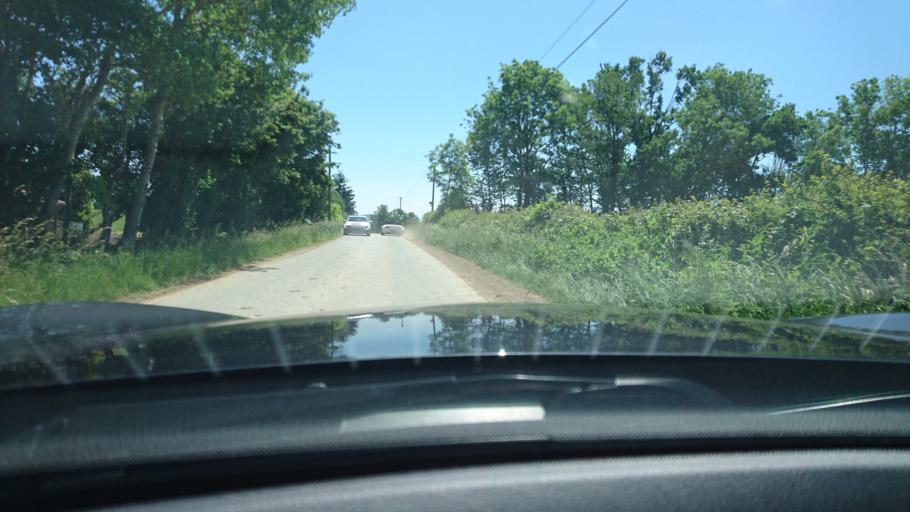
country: FR
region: Rhone-Alpes
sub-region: Departement de la Loire
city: Bussieres
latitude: 45.8255
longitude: 4.2999
